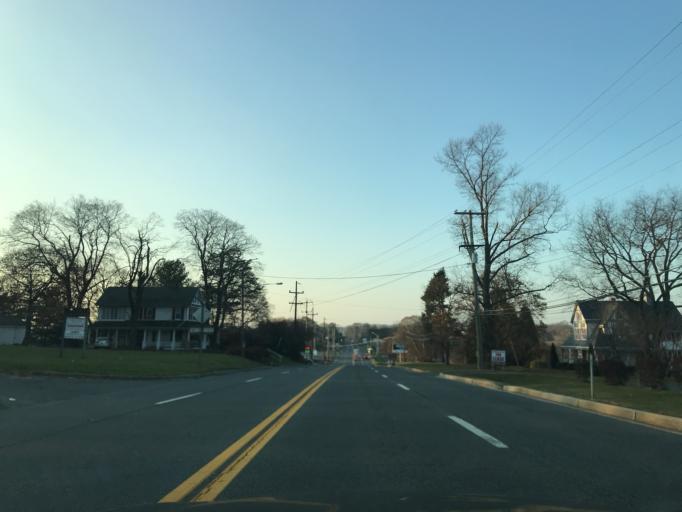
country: US
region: Pennsylvania
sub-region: York County
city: Susquehanna Trails
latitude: 39.7099
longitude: -76.3469
